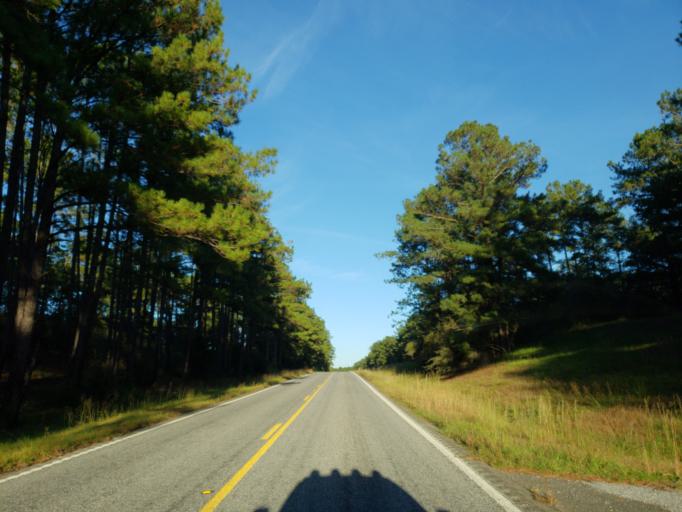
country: US
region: Mississippi
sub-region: Wayne County
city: Belmont
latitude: 31.4014
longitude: -88.6294
